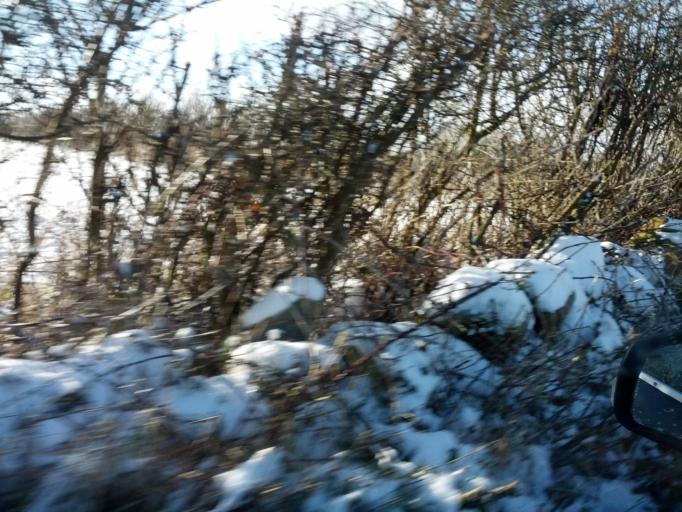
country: IE
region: Connaught
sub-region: County Galway
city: Athenry
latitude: 53.2096
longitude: -8.8161
